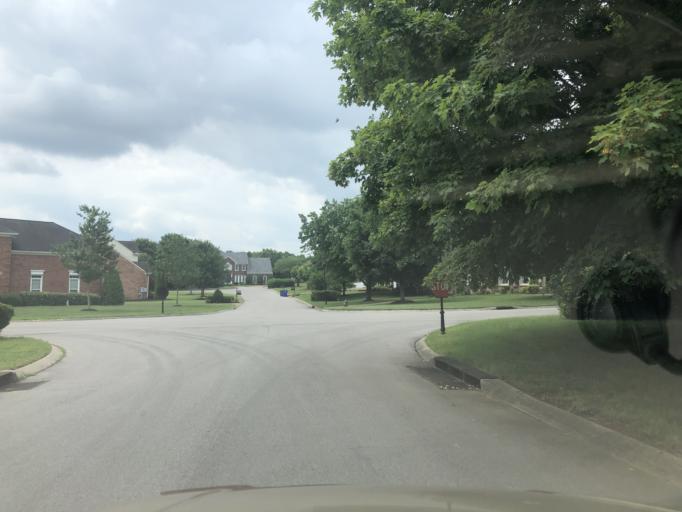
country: US
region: Tennessee
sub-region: Davidson County
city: Lakewood
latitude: 36.2325
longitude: -86.6054
